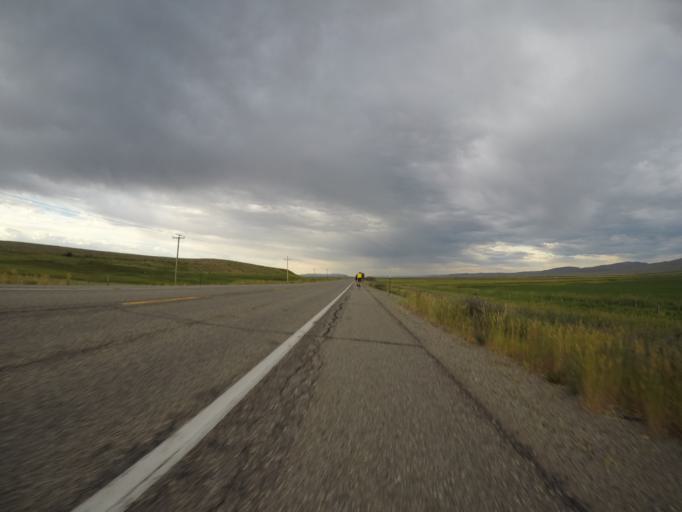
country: US
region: Utah
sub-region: Rich County
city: Randolph
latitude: 41.9742
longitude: -110.9449
